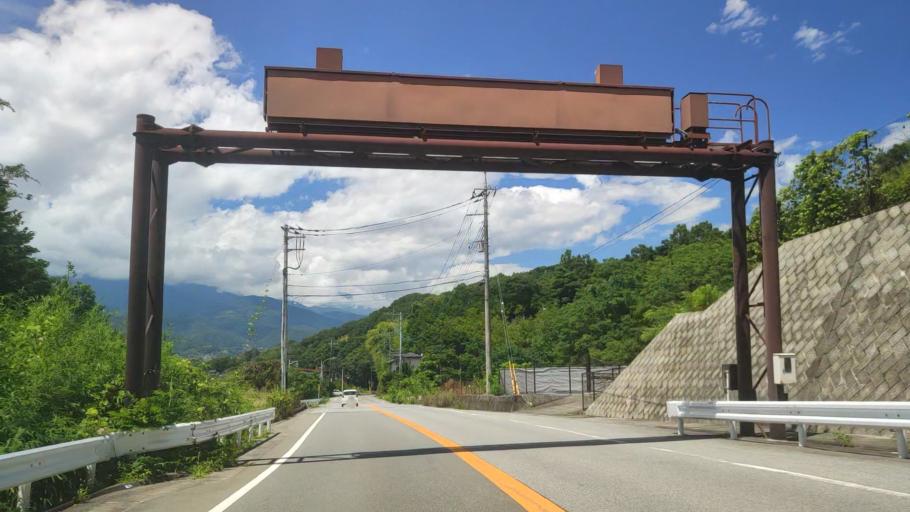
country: JP
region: Yamanashi
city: Ryuo
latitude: 35.5274
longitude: 138.4833
